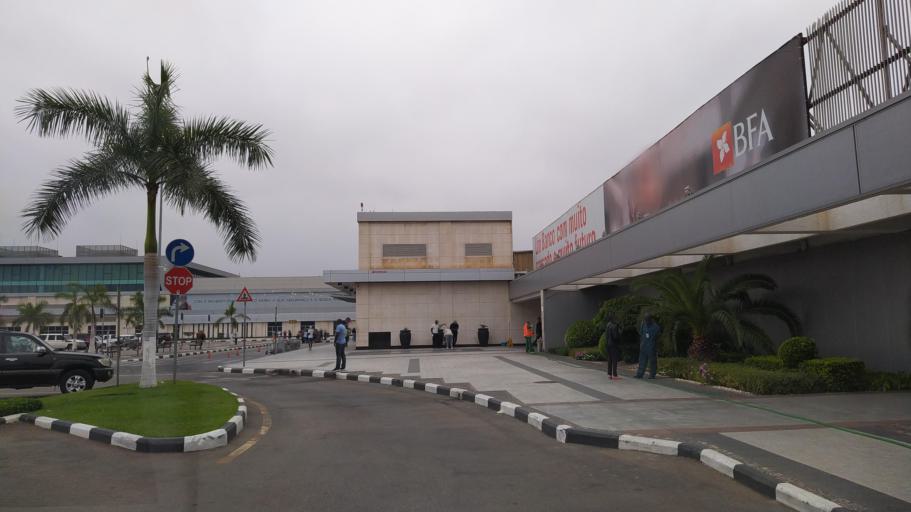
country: AO
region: Luanda
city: Luanda
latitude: -8.8480
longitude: 13.2346
